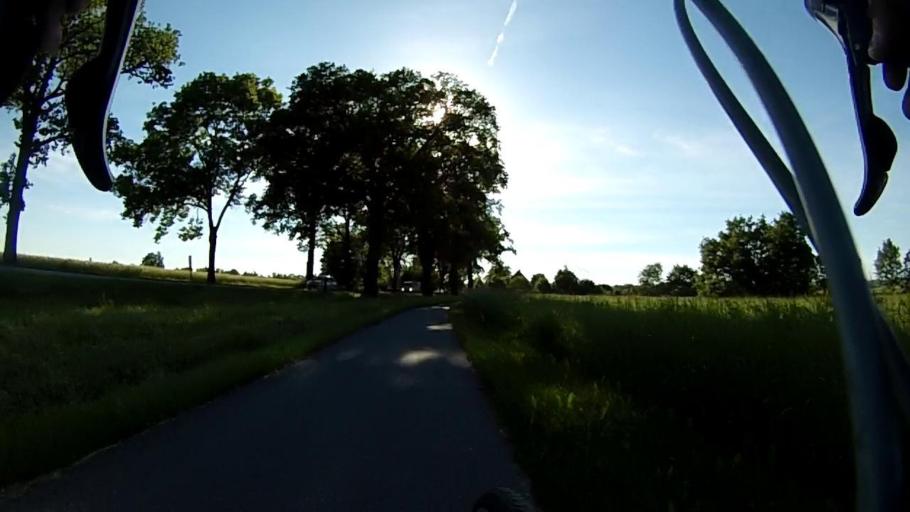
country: DE
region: Brandenburg
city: Werneuchen
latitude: 52.6216
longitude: 13.6905
